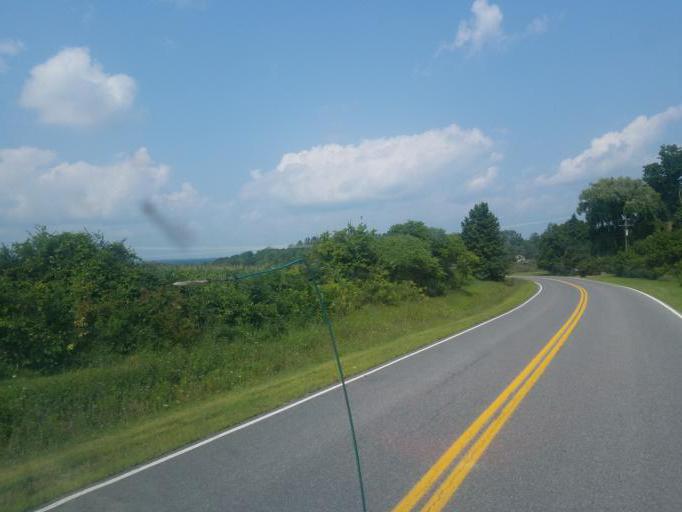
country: US
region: New York
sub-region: Montgomery County
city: Tribes Hill
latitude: 42.9121
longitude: -74.3292
